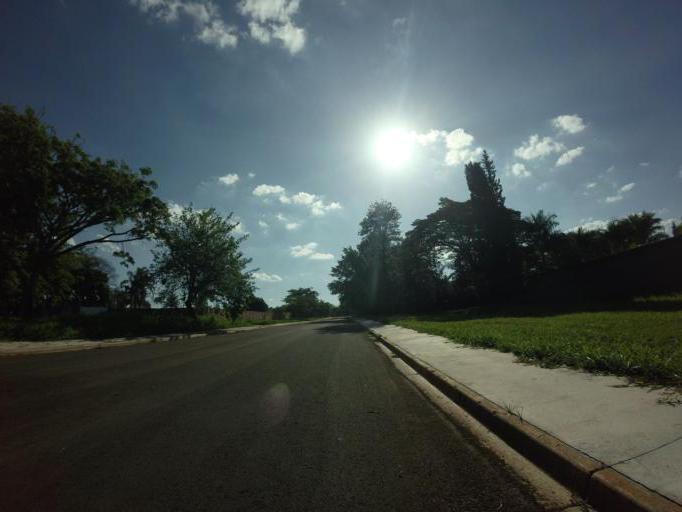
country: BR
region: Sao Paulo
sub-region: Piracicaba
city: Piracicaba
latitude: -22.7580
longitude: -47.5917
